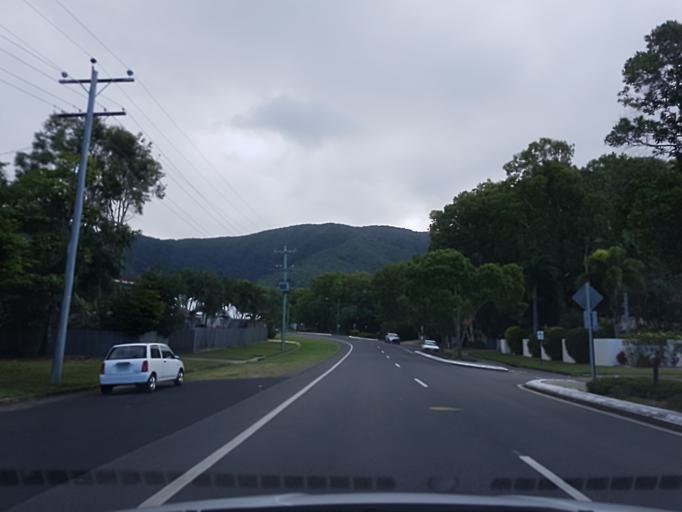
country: AU
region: Queensland
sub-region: Cairns
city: Palm Cove
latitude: -16.7614
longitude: 145.6725
